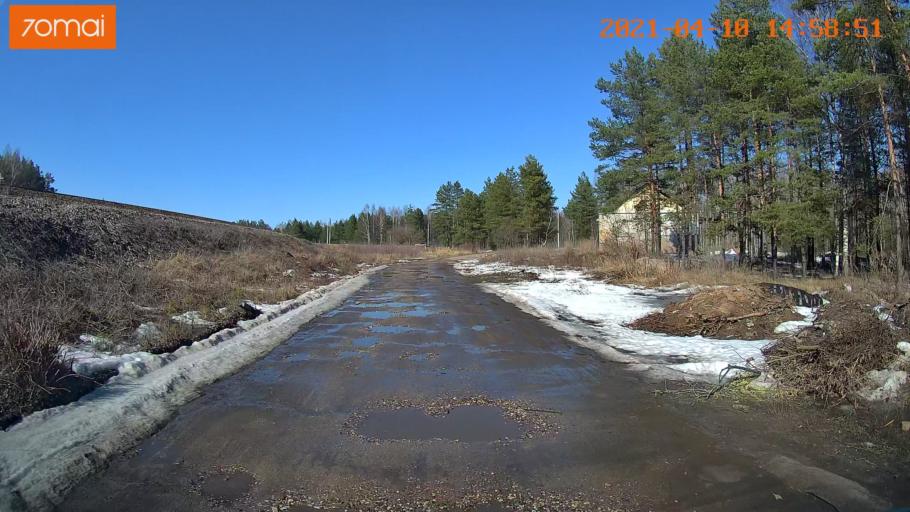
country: RU
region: Ivanovo
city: Bogorodskoye
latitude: 56.9962
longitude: 41.0599
